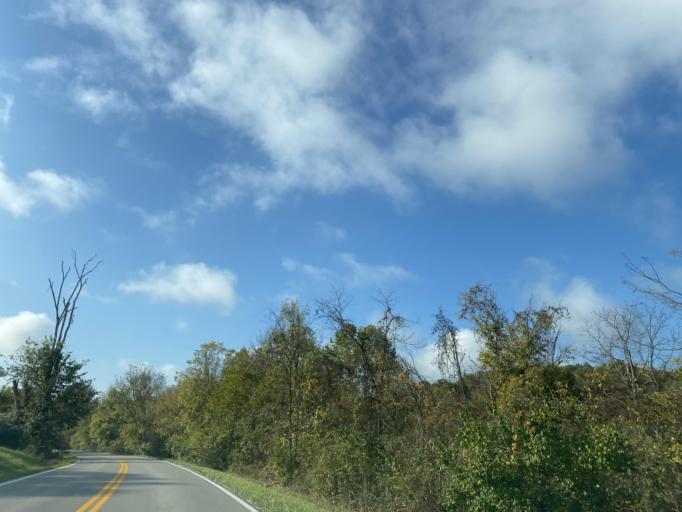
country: US
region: Kentucky
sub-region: Pendleton County
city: Falmouth
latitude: 38.7061
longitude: -84.3038
